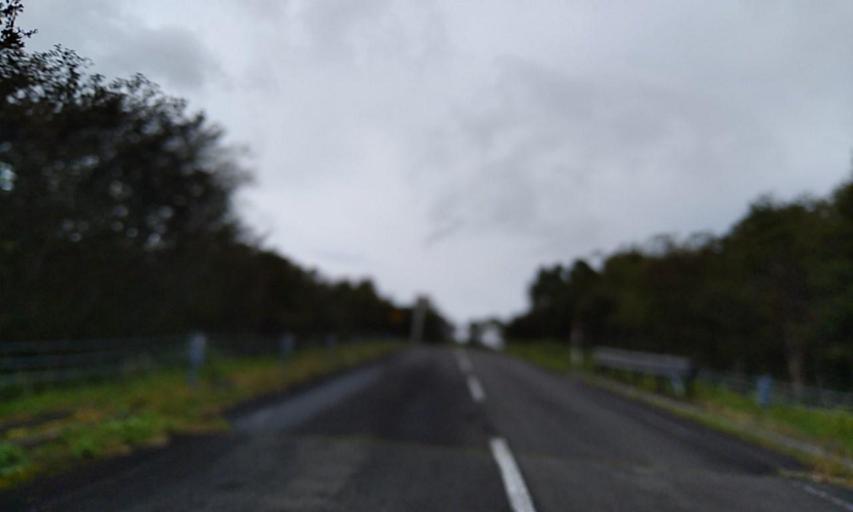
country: JP
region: Hokkaido
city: Abashiri
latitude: 43.6014
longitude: 144.5723
